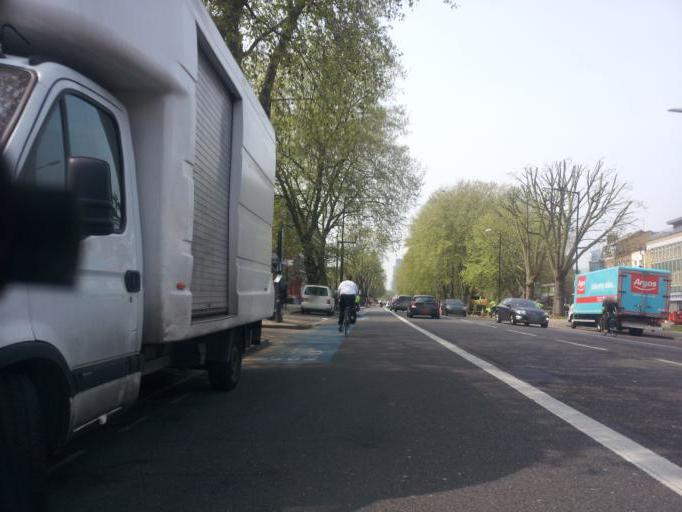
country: GB
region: England
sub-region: Greater London
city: Bethnal Green
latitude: 51.5209
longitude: -0.0513
